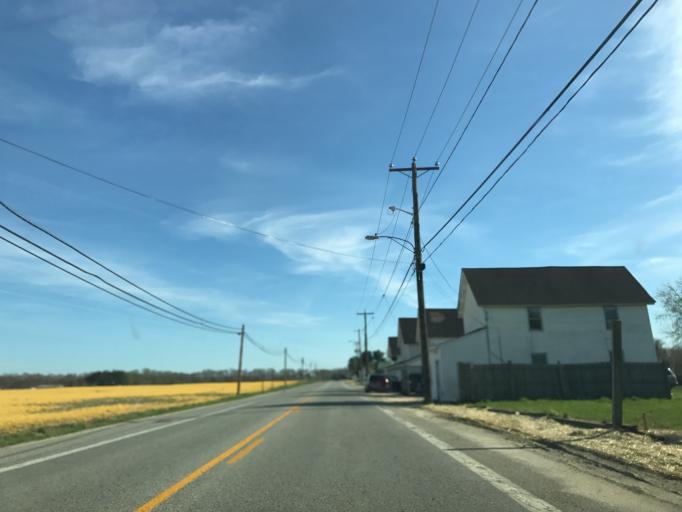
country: US
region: Maryland
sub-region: Caroline County
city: Greensboro
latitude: 39.0323
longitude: -75.7869
